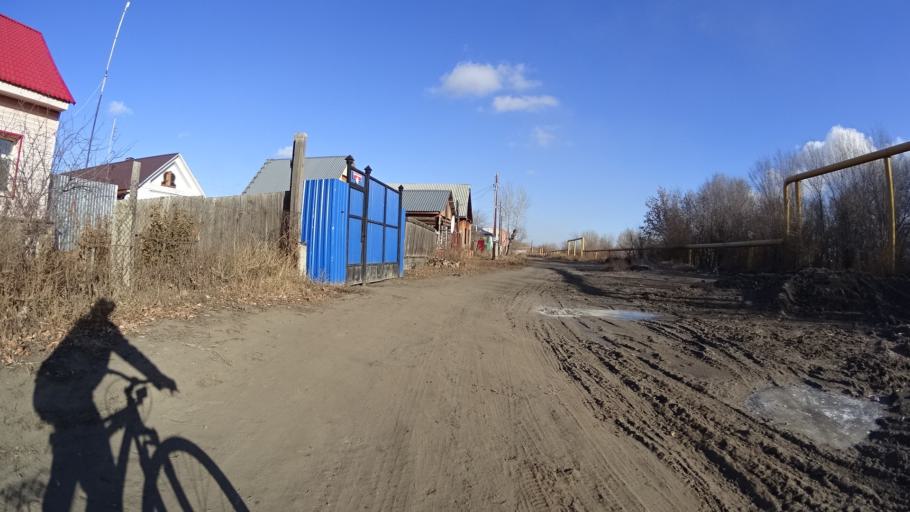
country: RU
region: Chelyabinsk
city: Troitsk
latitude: 54.0822
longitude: 61.5697
